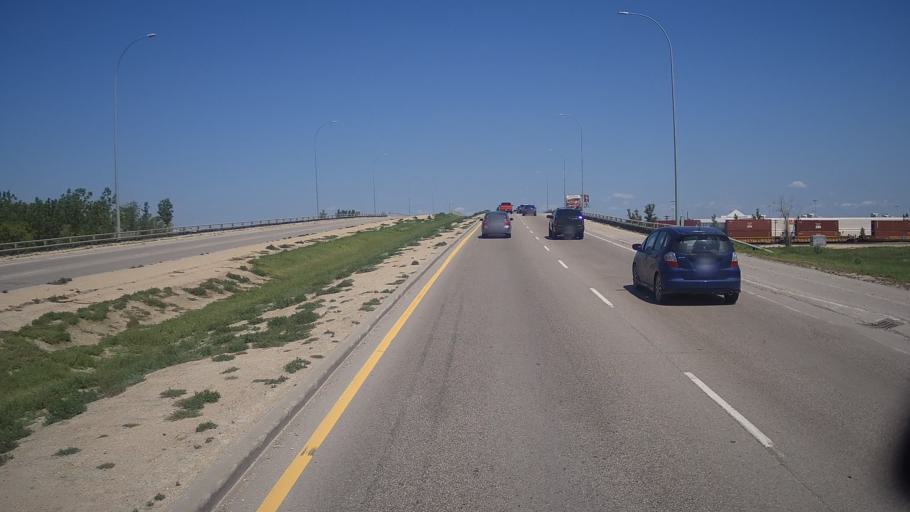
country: CA
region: Manitoba
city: Winnipeg
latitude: 49.8923
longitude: -97.0715
